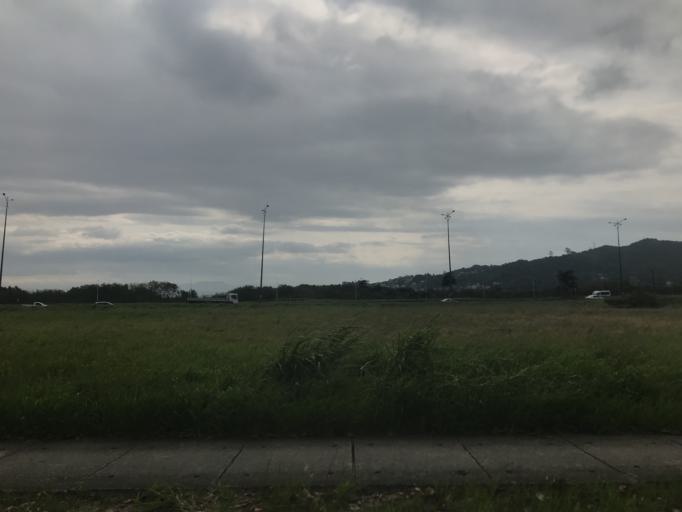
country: BR
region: Santa Catarina
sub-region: Florianopolis
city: Saco dos Limoes
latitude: -27.6186
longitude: -48.5271
